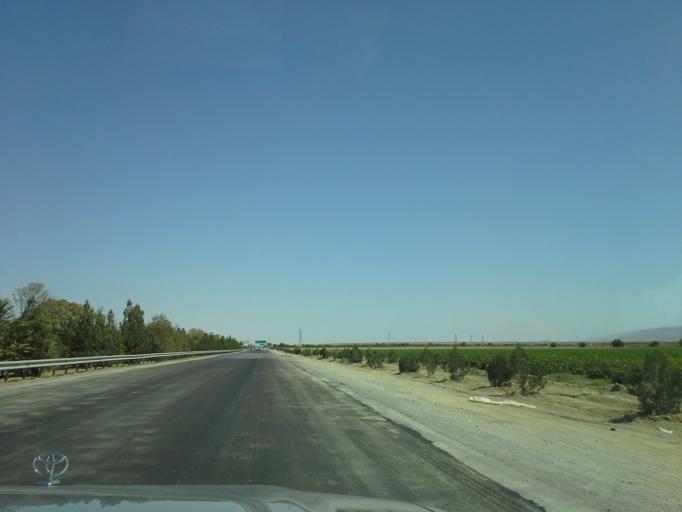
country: TM
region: Ahal
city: Annau
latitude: 37.9058
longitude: 58.5314
